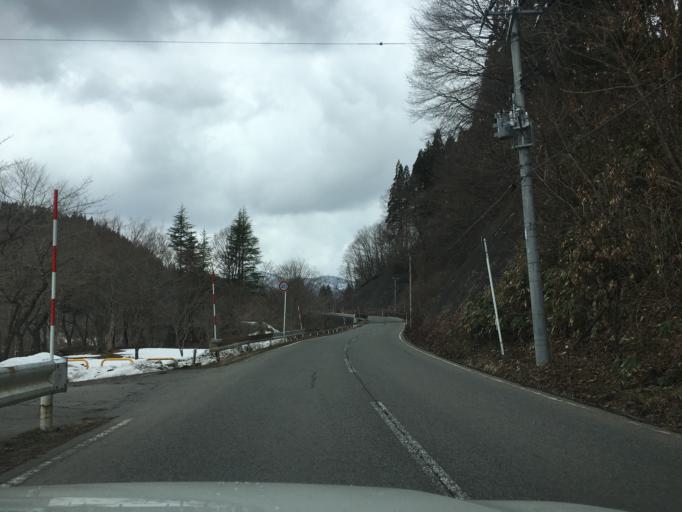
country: JP
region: Akita
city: Odate
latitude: 40.4258
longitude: 140.6561
